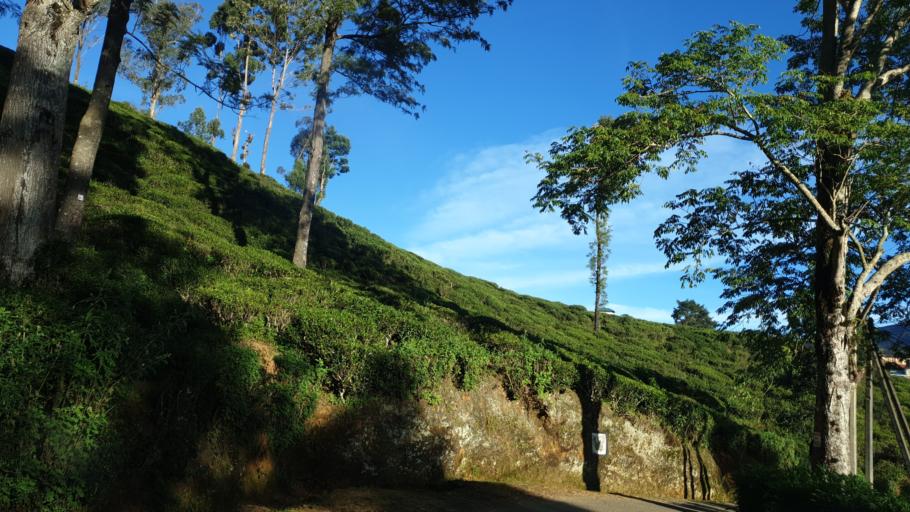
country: LK
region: Central
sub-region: Nuwara Eliya District
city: Nuwara Eliya
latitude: 6.9591
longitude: 80.7656
